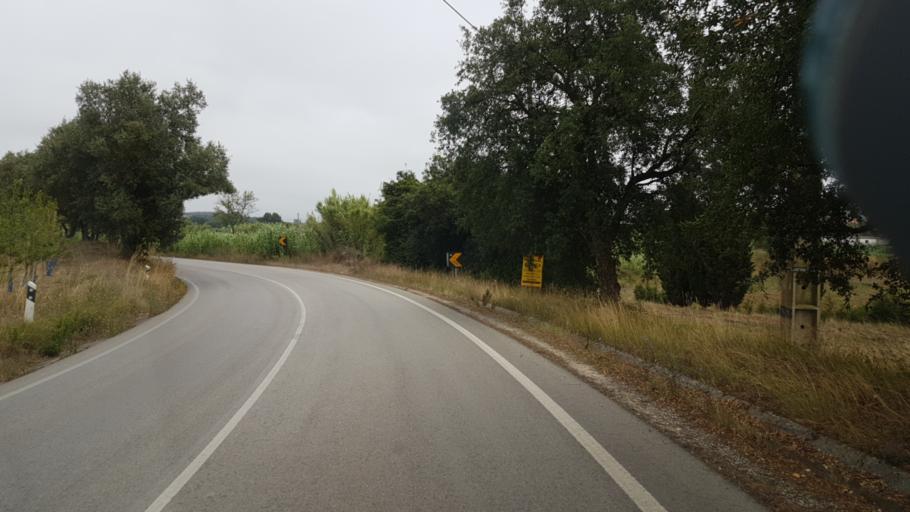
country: PT
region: Leiria
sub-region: Bombarral
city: Bombarral
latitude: 39.2761
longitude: -9.1567
